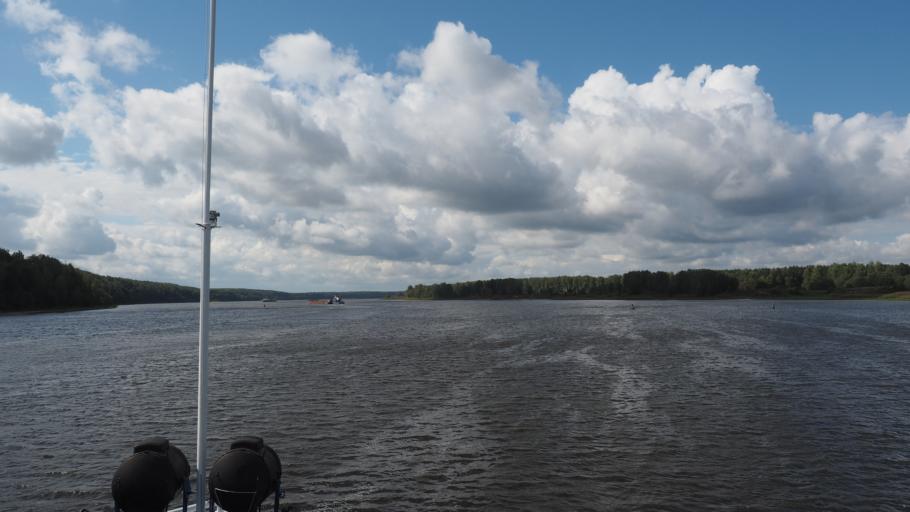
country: RU
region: Jaroslavl
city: Tutayev
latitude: 57.9310
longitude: 39.4394
